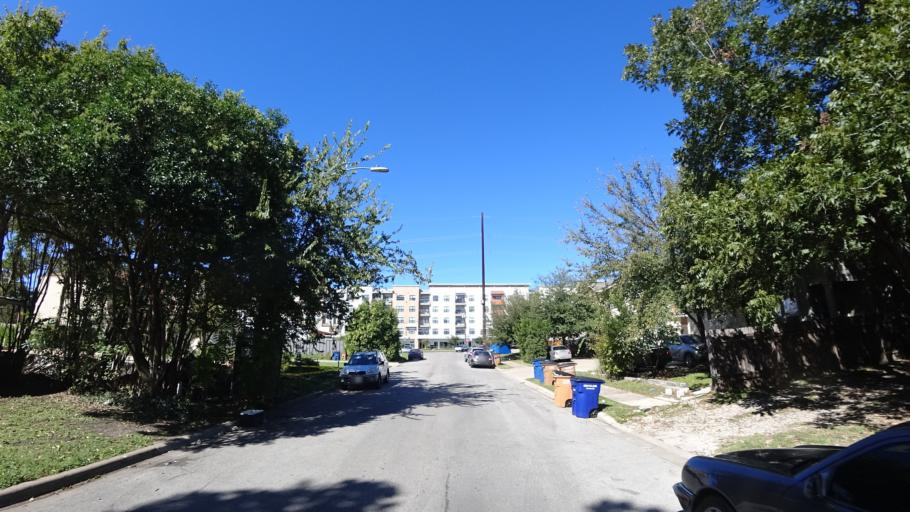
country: US
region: Texas
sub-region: Travis County
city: Austin
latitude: 30.3216
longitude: -97.7279
